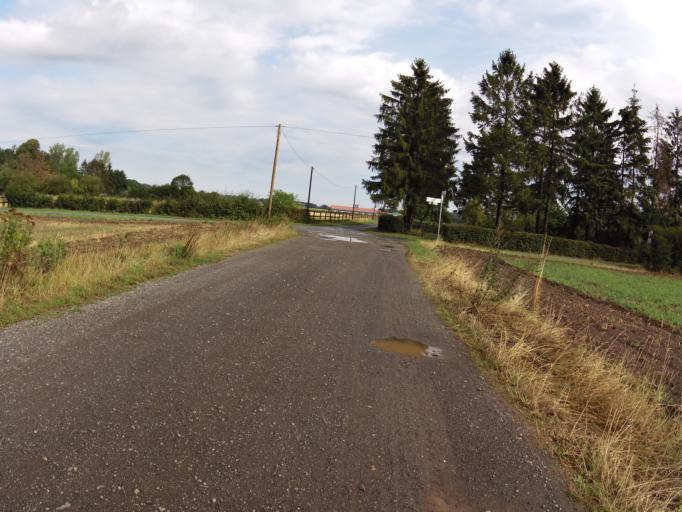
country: DE
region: Lower Saxony
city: Marklohe
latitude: 52.6713
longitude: 9.1682
